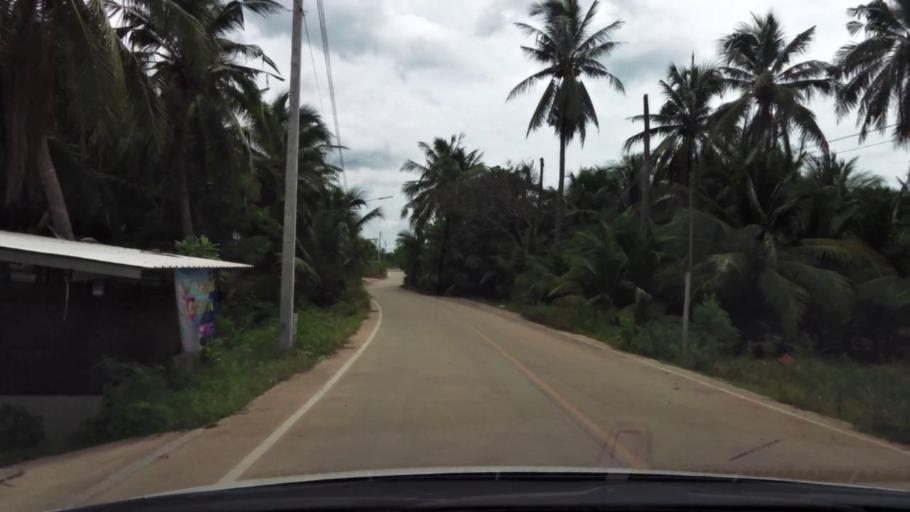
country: TH
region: Ratchaburi
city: Damnoen Saduak
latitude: 13.5517
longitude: 100.0247
